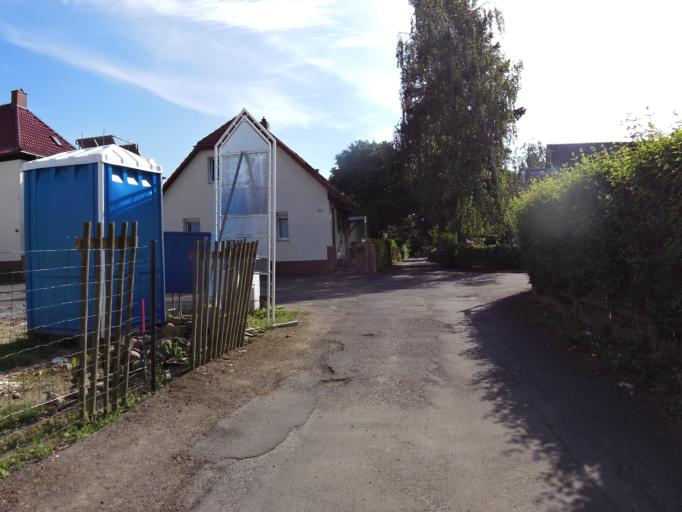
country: DE
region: Saxony
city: Leipzig
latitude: 51.3125
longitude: 12.4269
